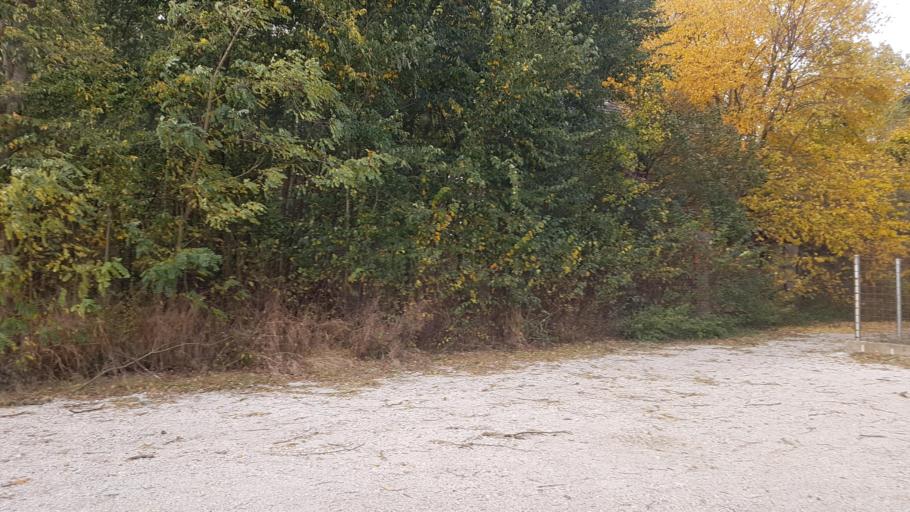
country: DE
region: Brandenburg
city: Schraden
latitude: 51.4484
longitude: 13.7154
